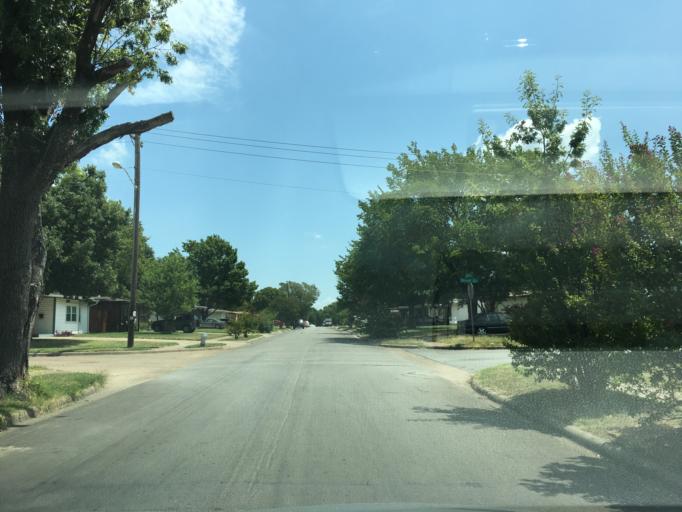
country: US
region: Texas
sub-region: Dallas County
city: Garland
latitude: 32.8600
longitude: -96.6792
